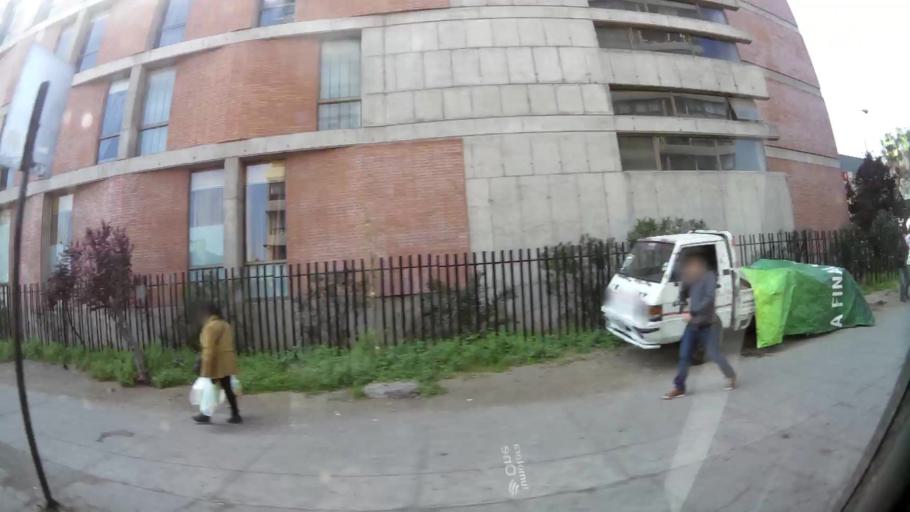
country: CL
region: Santiago Metropolitan
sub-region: Provincia de Santiago
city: Santiago
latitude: -33.4531
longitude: -70.6526
